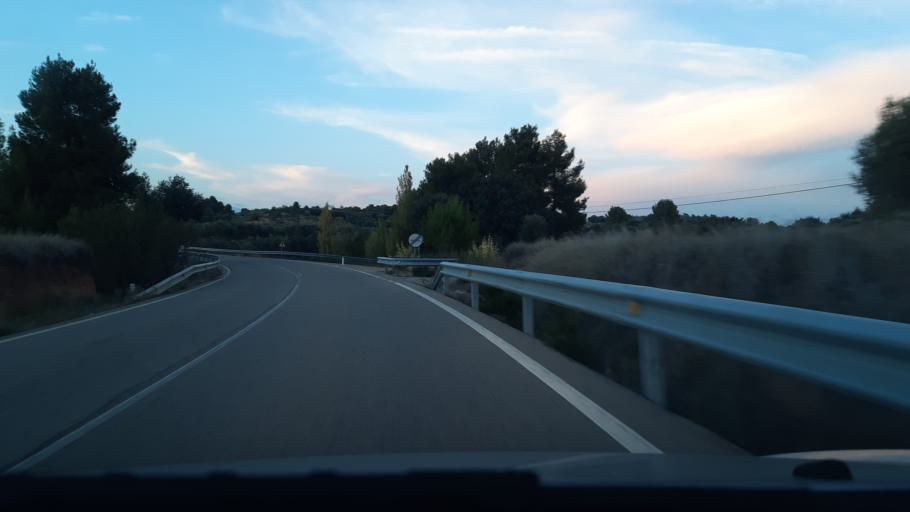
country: ES
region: Aragon
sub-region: Provincia de Teruel
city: Valderrobres
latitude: 40.8515
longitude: 0.1738
